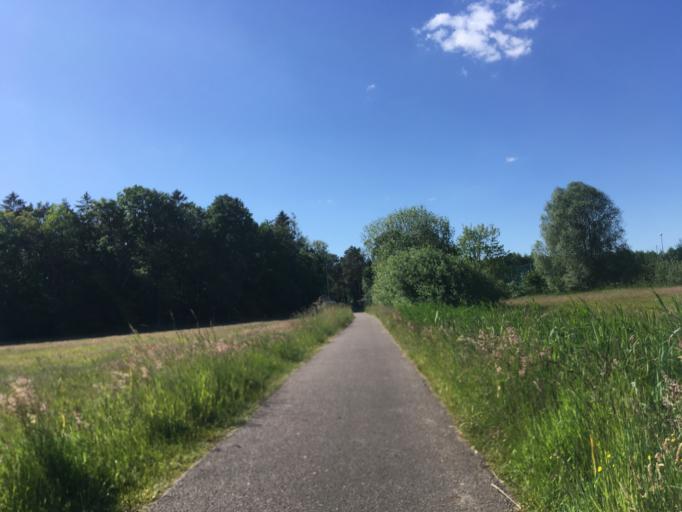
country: DE
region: Brandenburg
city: Althuttendorf
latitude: 52.9622
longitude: 13.7982
